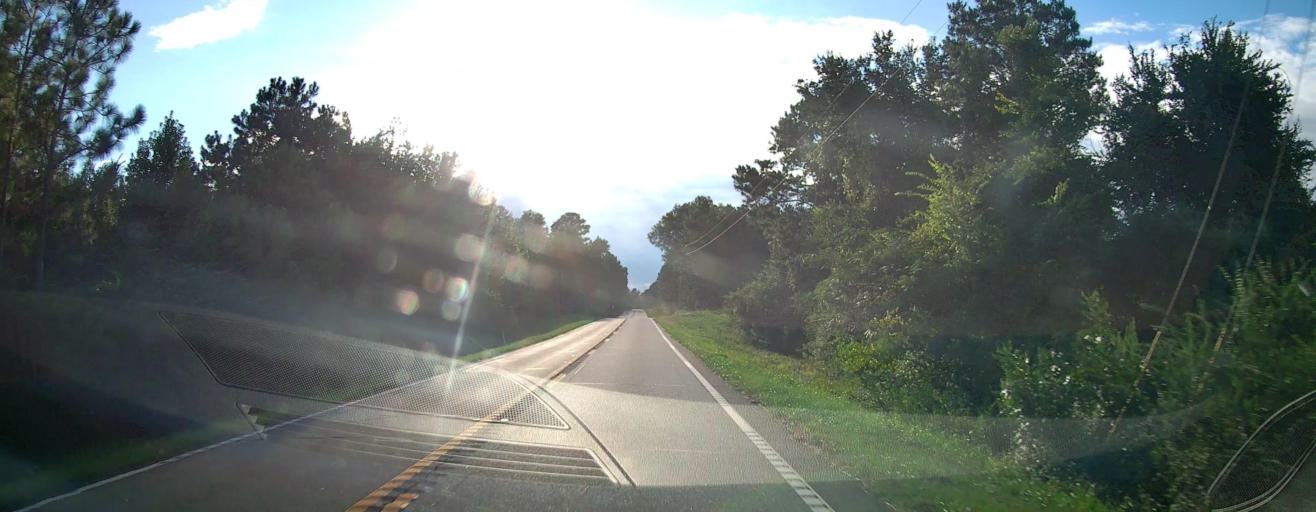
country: US
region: Georgia
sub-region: Pulaski County
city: Hawkinsville
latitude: 32.2659
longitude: -83.5288
